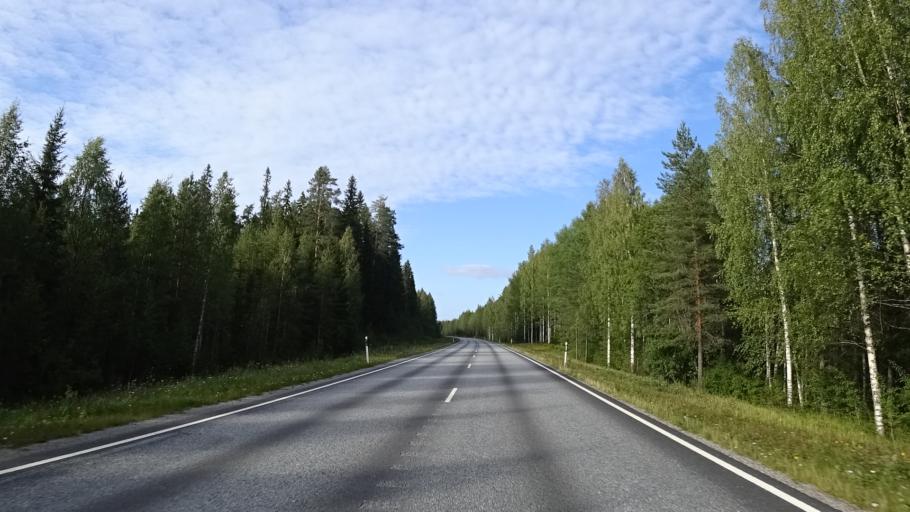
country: FI
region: North Karelia
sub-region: Joensuu
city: Eno
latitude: 62.8206
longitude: 30.1896
